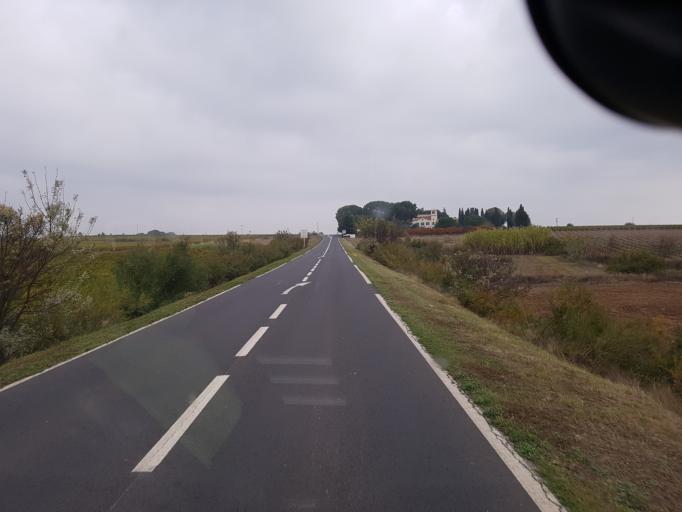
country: FR
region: Languedoc-Roussillon
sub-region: Departement de l'Herault
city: Marseillan
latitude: 43.3863
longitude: 3.5366
